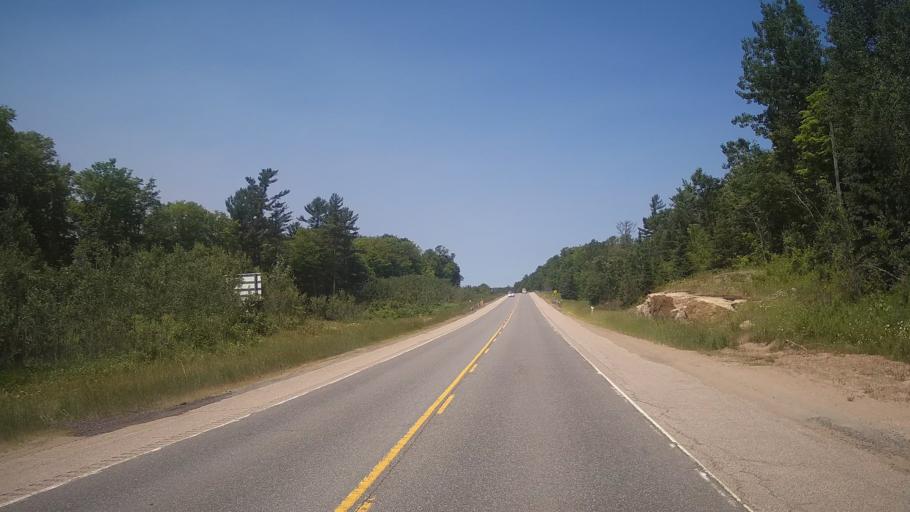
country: CA
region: Ontario
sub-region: Parry Sound District
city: Parry Sound
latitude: 45.4770
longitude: -80.1781
